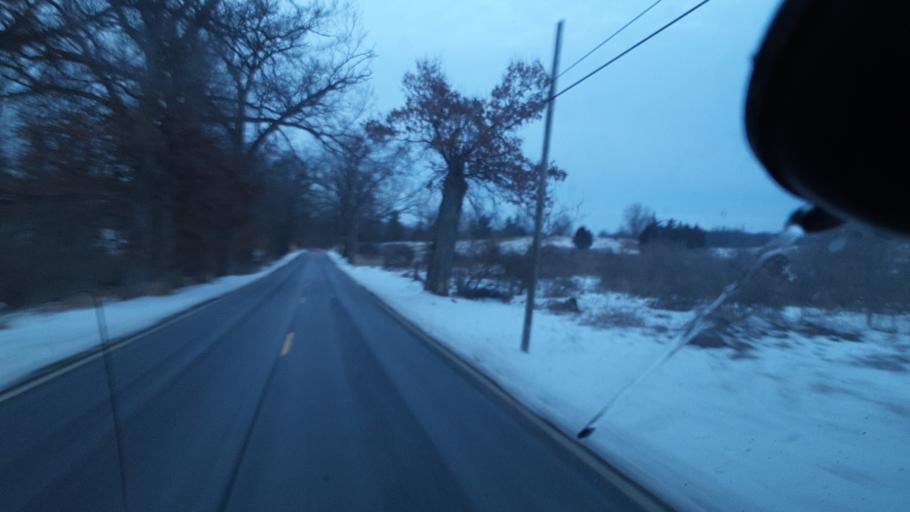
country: US
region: Michigan
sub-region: Jackson County
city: Grass Lake
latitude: 42.3150
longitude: -84.2096
